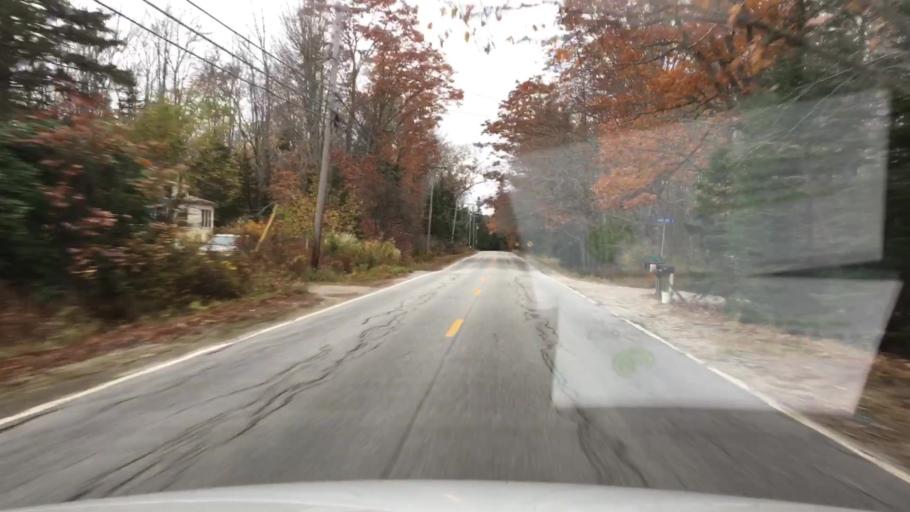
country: US
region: Maine
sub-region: Hancock County
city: Sedgwick
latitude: 44.3656
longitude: -68.5528
